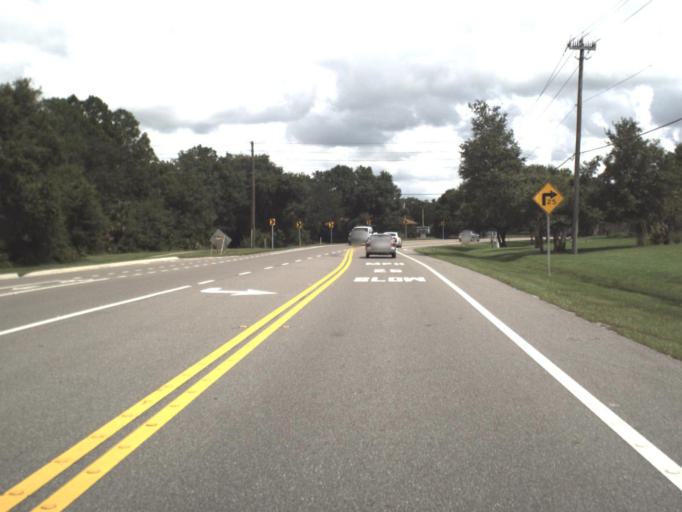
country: US
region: Florida
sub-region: Sarasota County
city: Lake Sarasota
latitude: 27.2689
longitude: -82.4207
